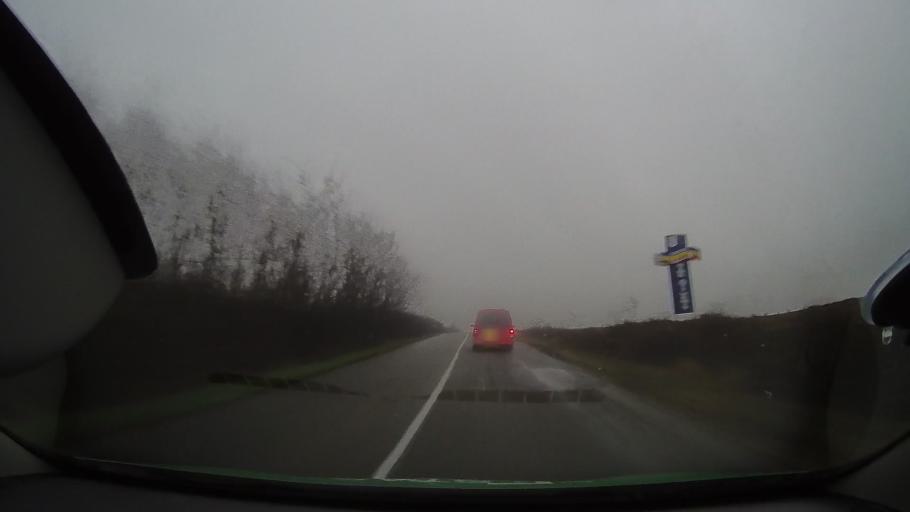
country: RO
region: Arad
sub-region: Comuna Craiova
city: Craiova
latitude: 46.6158
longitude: 21.9572
